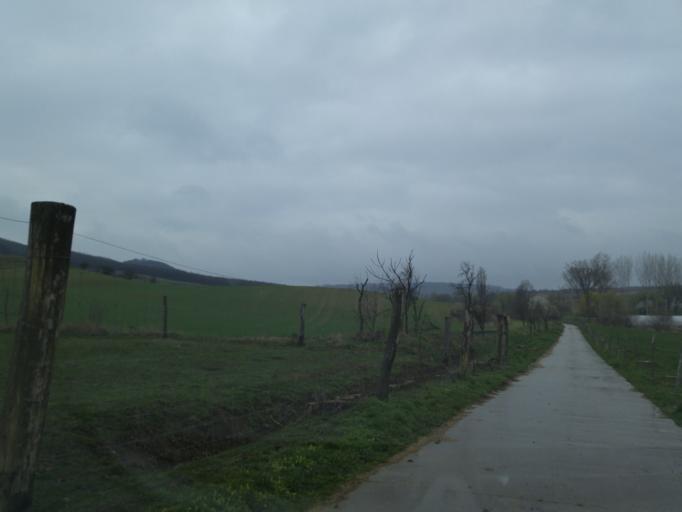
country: HU
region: Somogy
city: Adand
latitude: 46.8013
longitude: 18.1107
